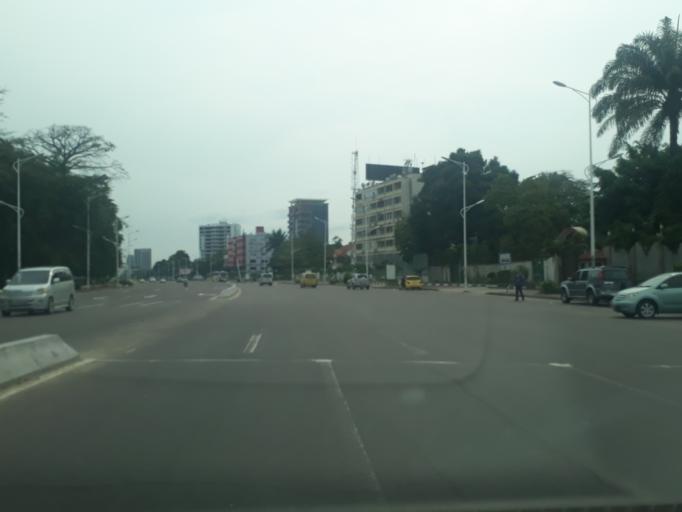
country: CD
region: Kinshasa
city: Kinshasa
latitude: -4.3071
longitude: 15.2950
